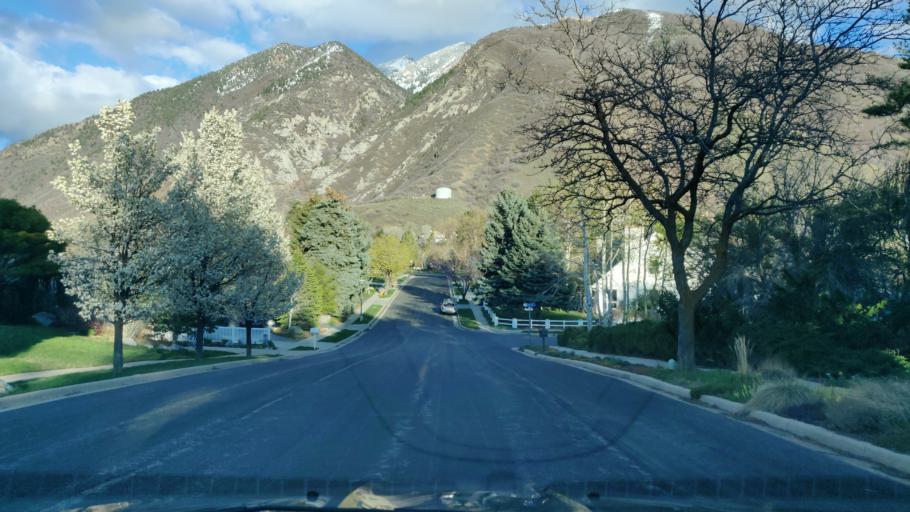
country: US
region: Utah
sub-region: Salt Lake County
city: Cottonwood Heights
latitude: 40.6152
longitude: -111.7936
